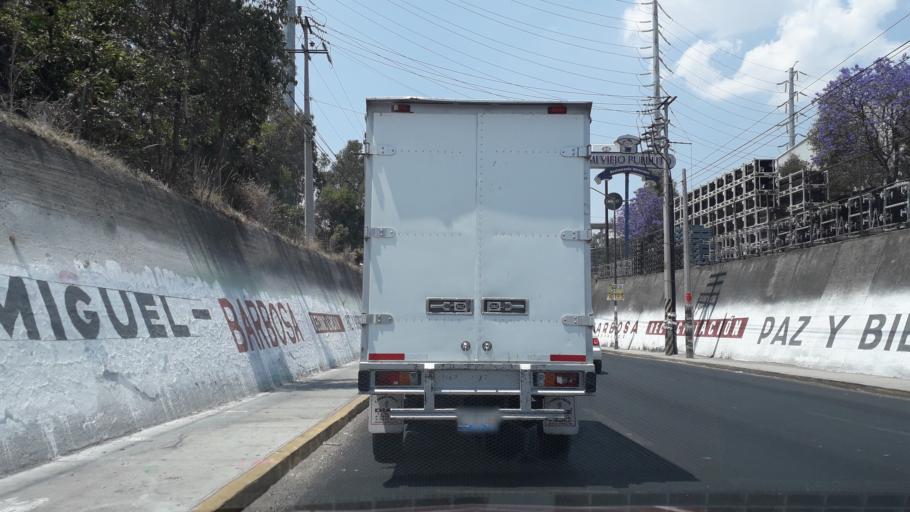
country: MX
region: Puebla
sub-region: Cuautlancingo
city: Sanctorum
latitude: 19.1115
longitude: -98.2478
